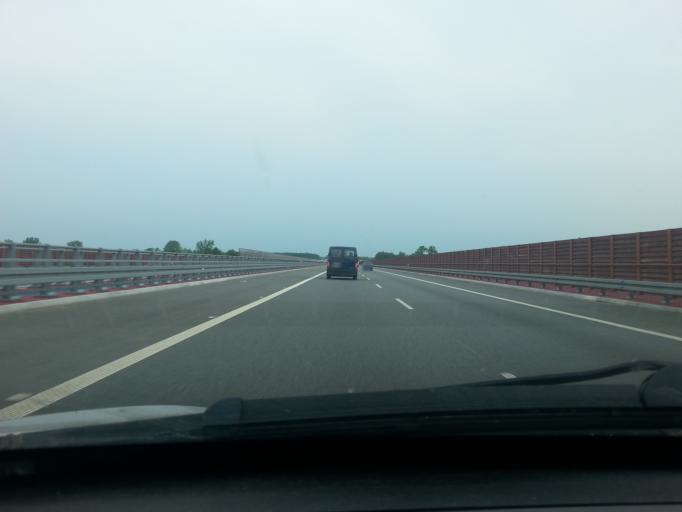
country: PL
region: Lodz Voivodeship
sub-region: Powiat skierniewicki
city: Bolimow
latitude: 52.0684
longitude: 20.1848
